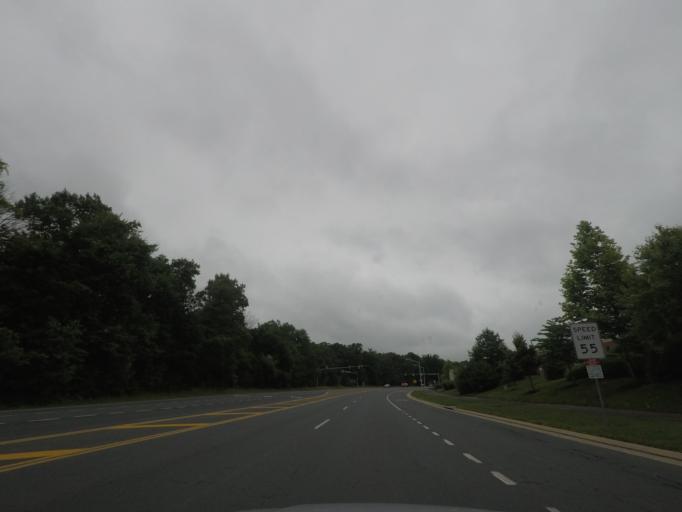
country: US
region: Virginia
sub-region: Prince William County
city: Haymarket
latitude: 38.7837
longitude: -77.6659
